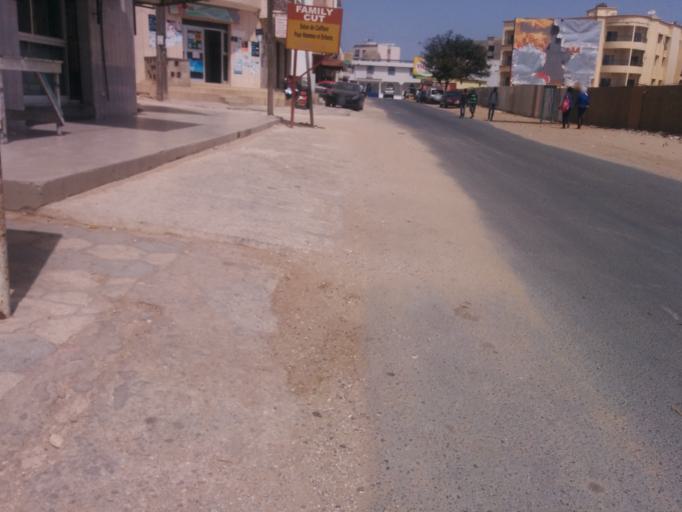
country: SN
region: Dakar
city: Grand Dakar
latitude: 14.7372
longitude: -17.4341
